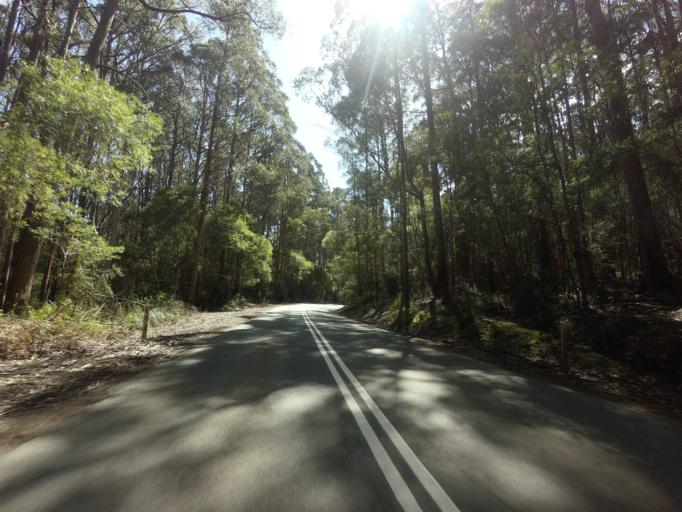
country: AU
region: Tasmania
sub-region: Derwent Valley
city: New Norfolk
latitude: -42.7364
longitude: 146.6646
